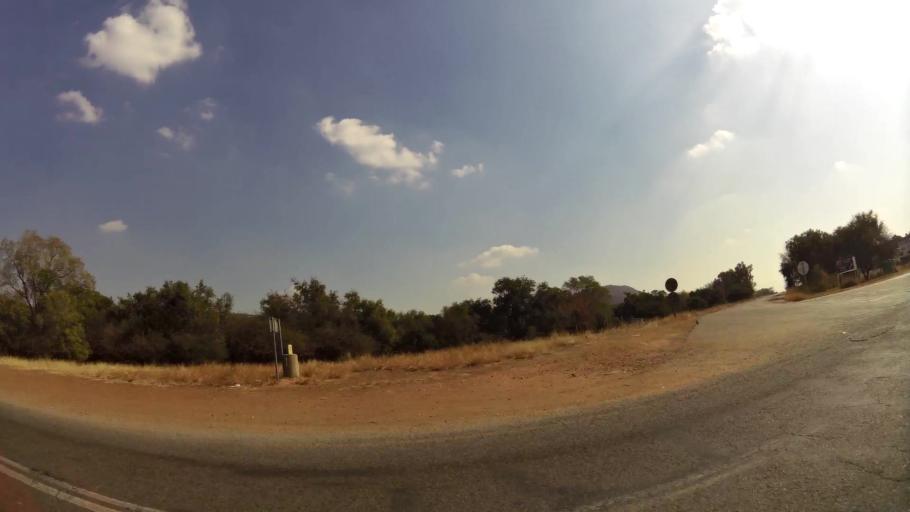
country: ZA
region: North-West
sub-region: Bojanala Platinum District Municipality
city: Rustenburg
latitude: -25.4927
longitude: 27.0857
